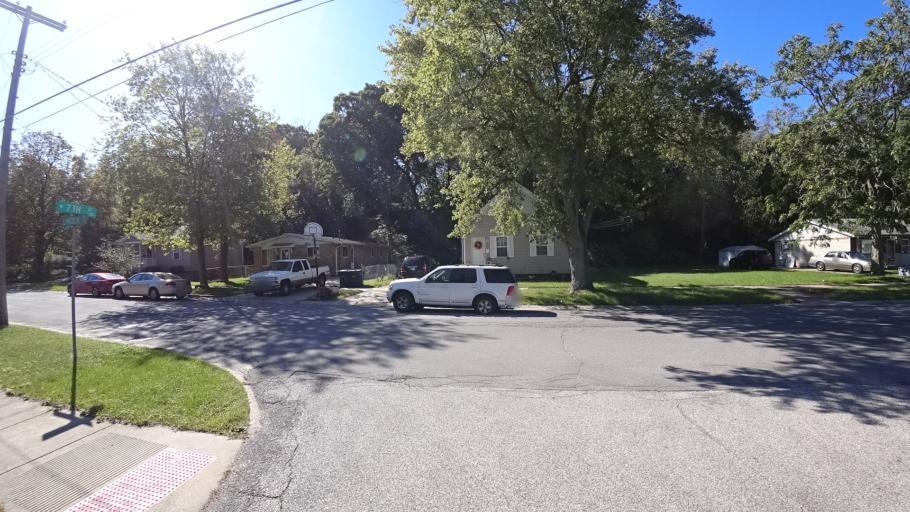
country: US
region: Indiana
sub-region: LaPorte County
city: Michigan City
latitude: 41.7104
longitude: -86.9162
